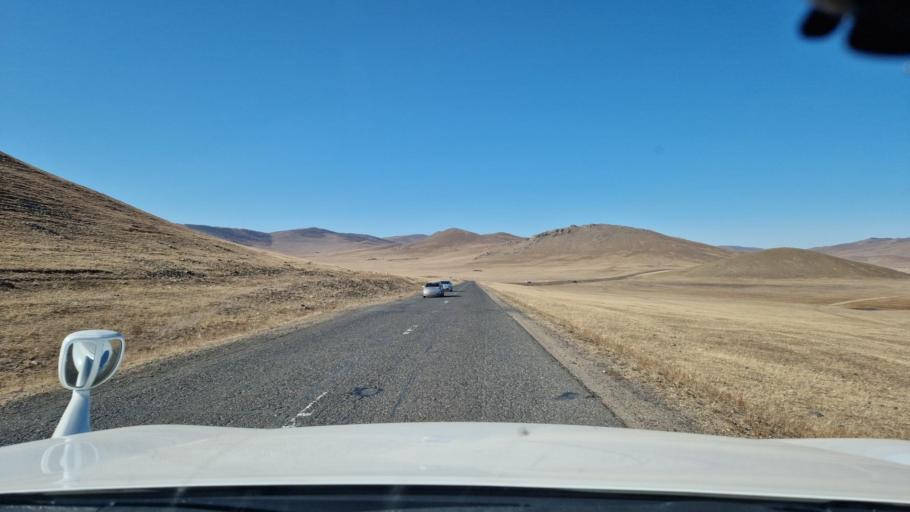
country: MN
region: Hentiy
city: Modot
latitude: 47.7528
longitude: 108.9533
